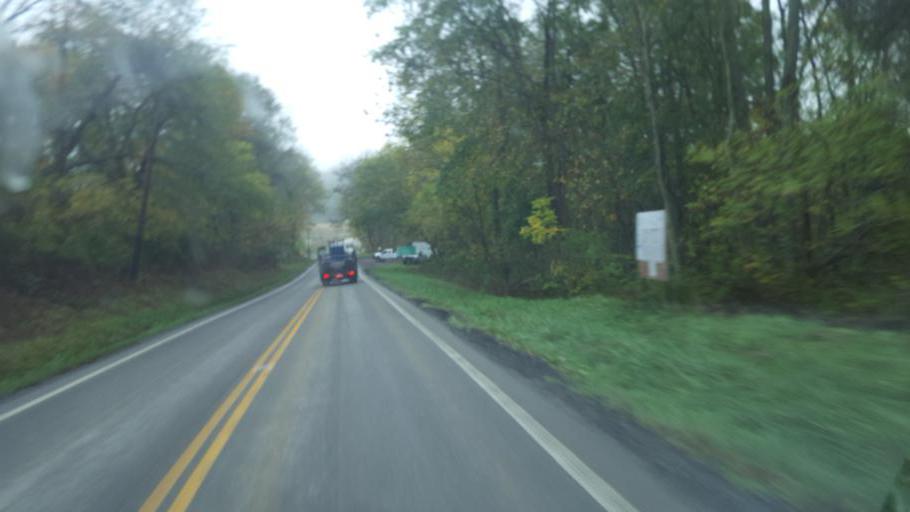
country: US
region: Ohio
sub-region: Carroll County
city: Carrollton
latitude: 40.4079
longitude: -81.1056
